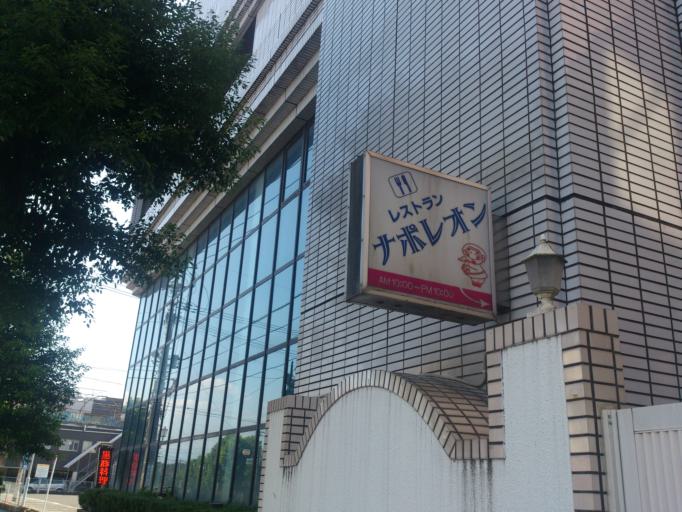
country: JP
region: Kagoshima
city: Kanoya
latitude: 31.3799
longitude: 130.8528
